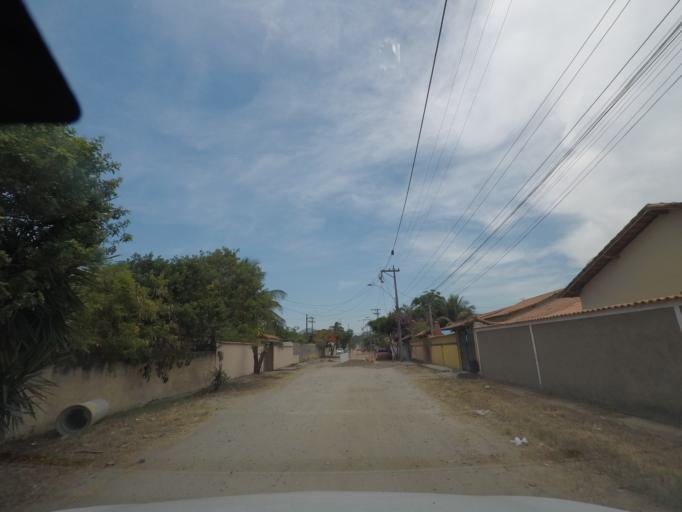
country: BR
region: Rio de Janeiro
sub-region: Niteroi
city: Niteroi
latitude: -22.9621
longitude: -42.9703
